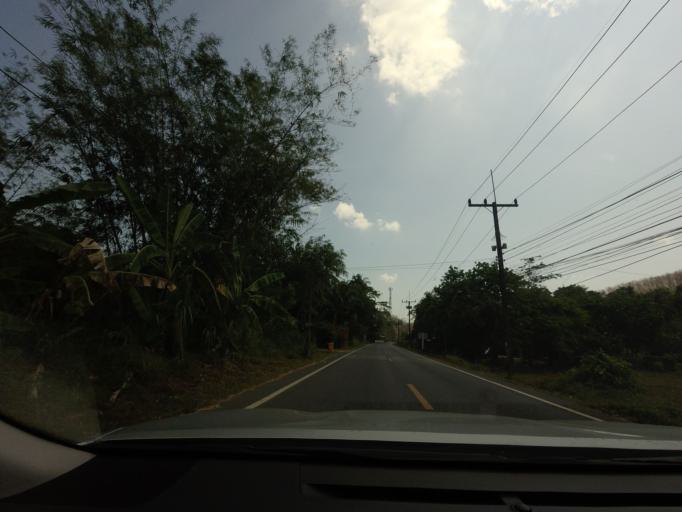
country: TH
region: Phangnga
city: Takua Thung
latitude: 8.2493
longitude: 98.3894
